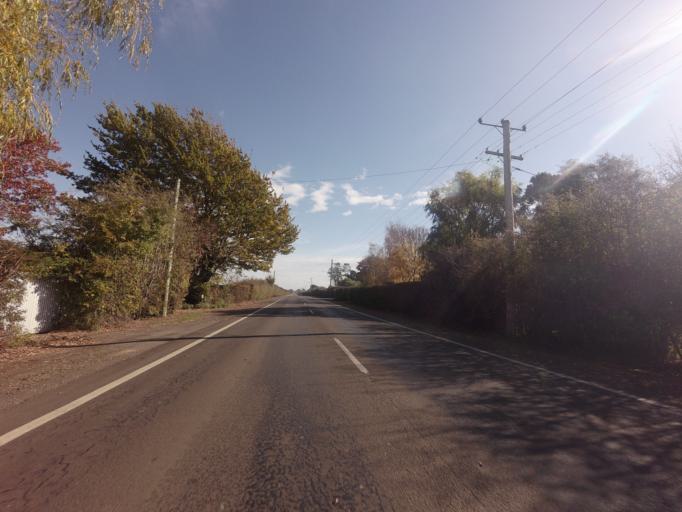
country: AU
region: Tasmania
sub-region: Meander Valley
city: Westbury
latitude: -41.5261
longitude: 146.8830
